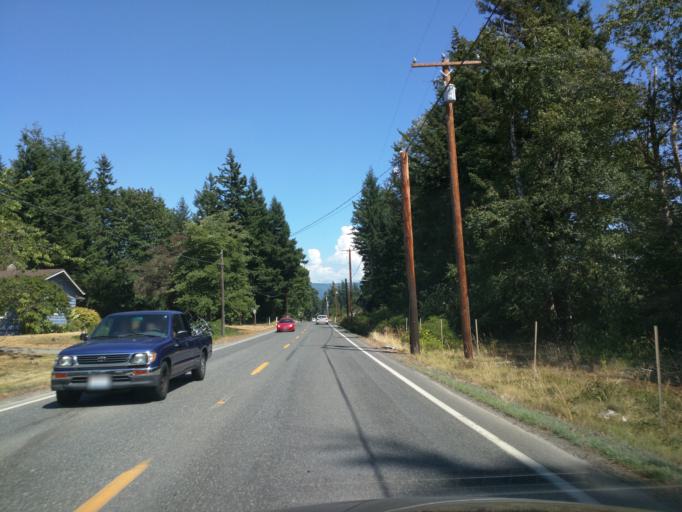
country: US
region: Washington
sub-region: Whatcom County
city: Everson
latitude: 48.8914
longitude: -122.3851
